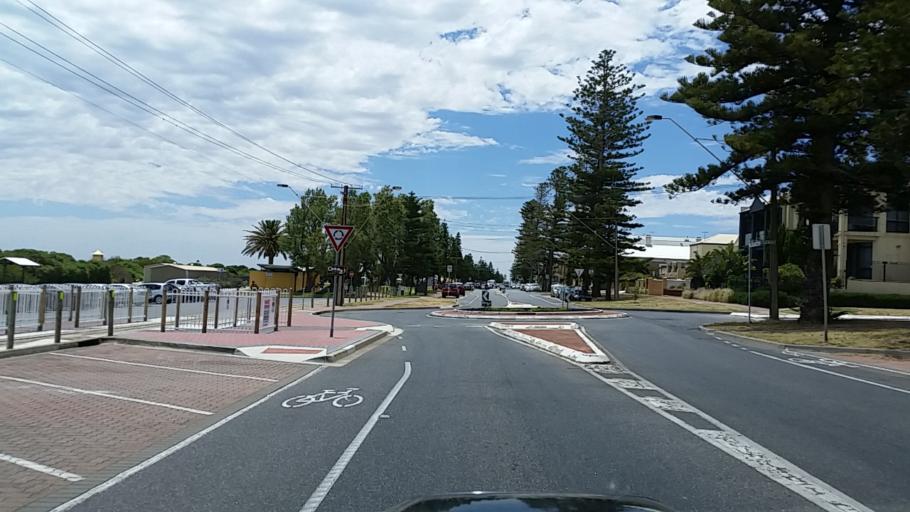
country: AU
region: South Australia
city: Port Adelaide
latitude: -34.8412
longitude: 138.4792
